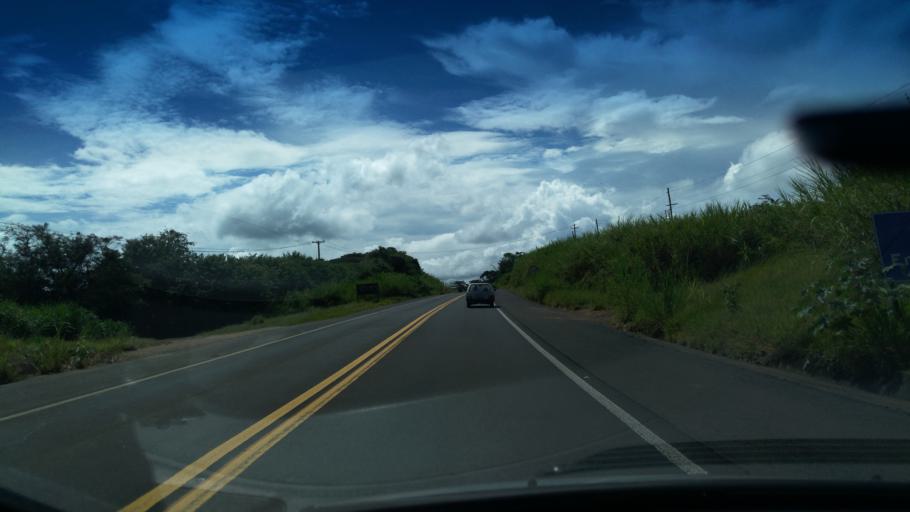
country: BR
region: Sao Paulo
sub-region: Santo Antonio Do Jardim
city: Espirito Santo do Pinhal
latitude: -22.1622
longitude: -46.7330
